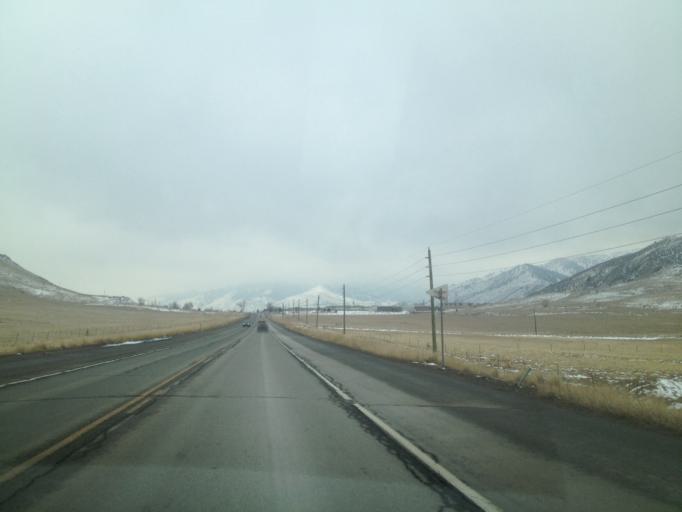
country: US
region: Colorado
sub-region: Jefferson County
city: Golden
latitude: 39.7899
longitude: -105.2307
